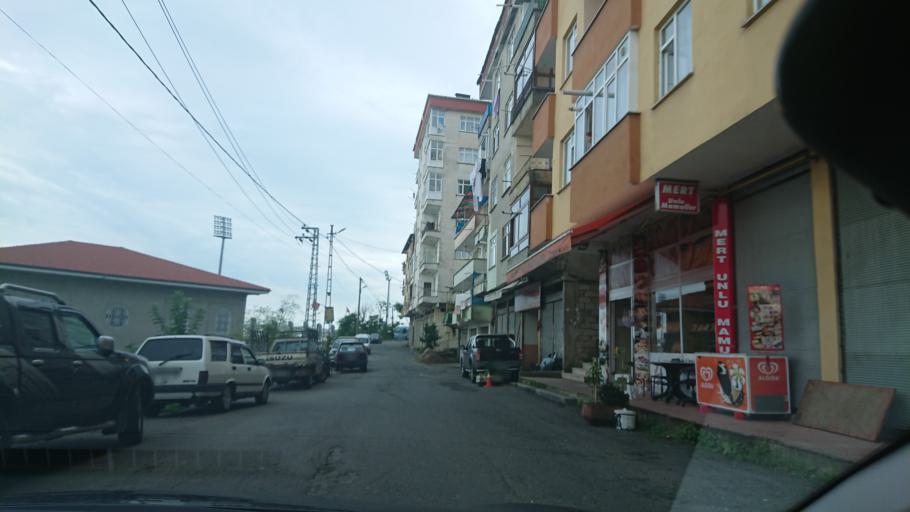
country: TR
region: Rize
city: Gundogdu
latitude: 41.0396
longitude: 40.5721
